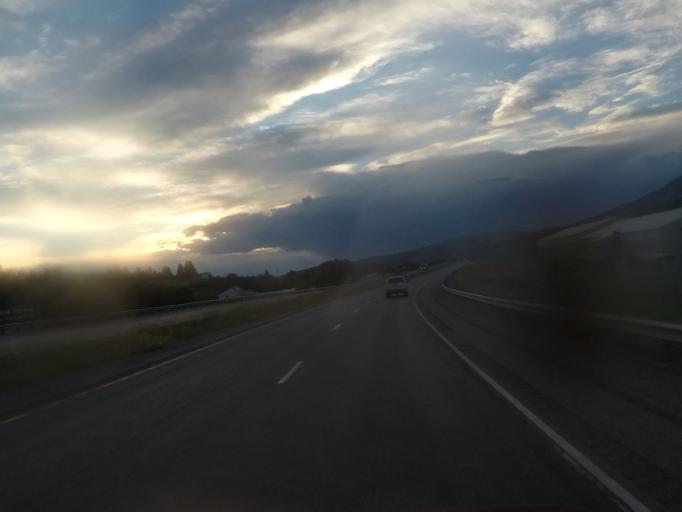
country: US
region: Montana
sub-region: Gallatin County
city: Bozeman
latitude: 45.6494
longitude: -110.9404
